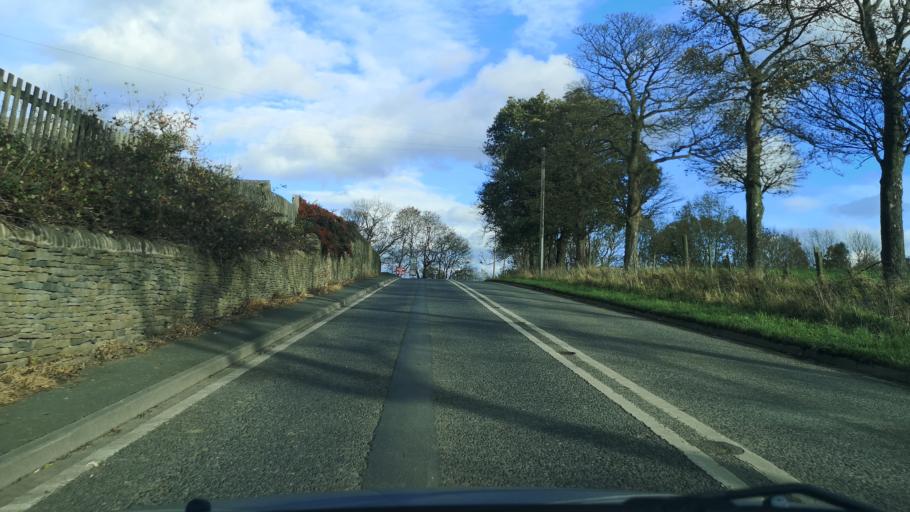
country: GB
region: England
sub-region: Kirklees
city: Shelley
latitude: 53.6368
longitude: -1.6559
